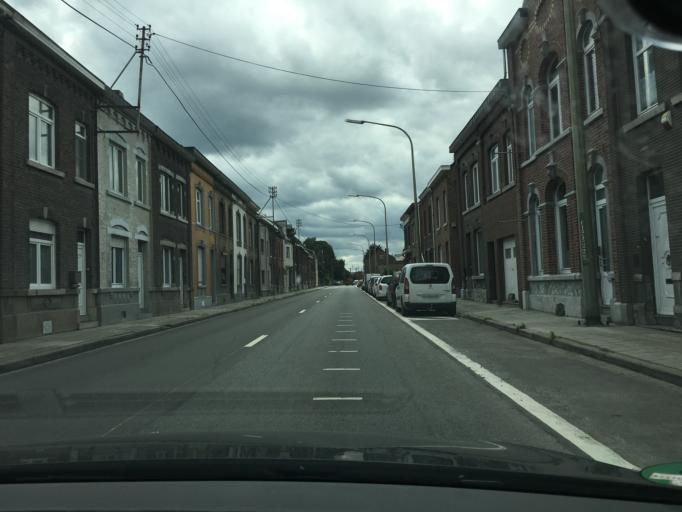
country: BE
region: Wallonia
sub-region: Province de Liege
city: Engis
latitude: 50.5854
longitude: 5.4140
